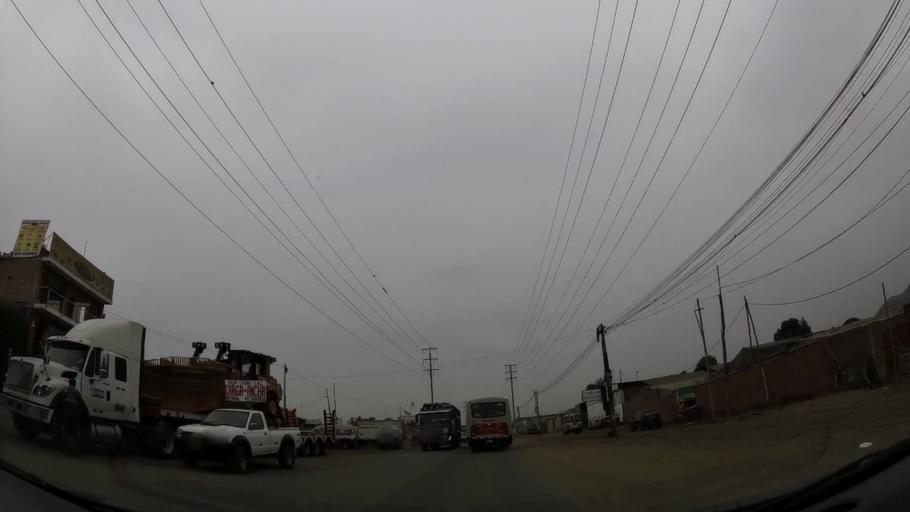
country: PE
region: Lima
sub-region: Lima
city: Punta Hermosa
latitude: -12.2697
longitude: -76.8762
